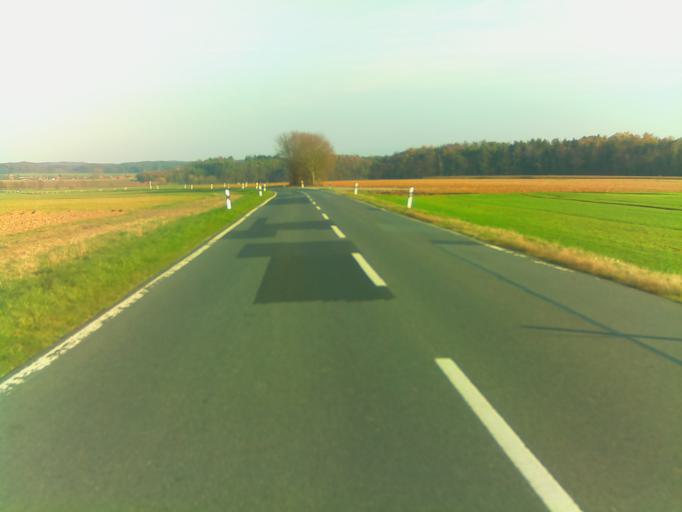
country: DE
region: Bavaria
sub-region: Regierungsbezirk Unterfranken
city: Neunkirchen
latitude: 49.7023
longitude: 9.3680
